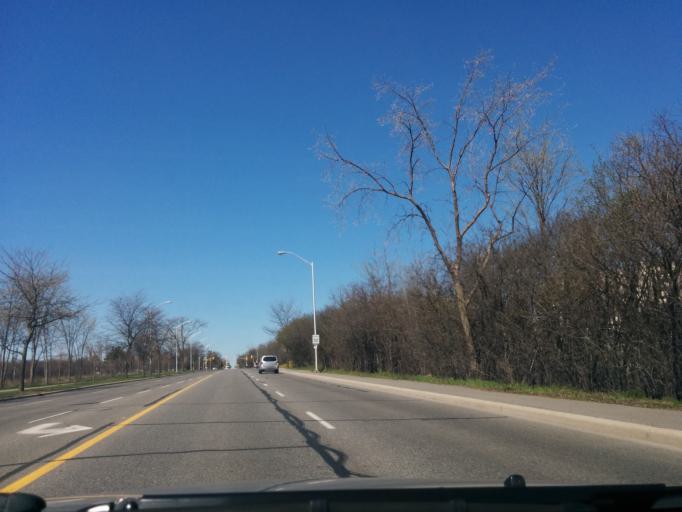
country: CA
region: Ontario
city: Ottawa
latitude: 45.3997
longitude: -75.6435
